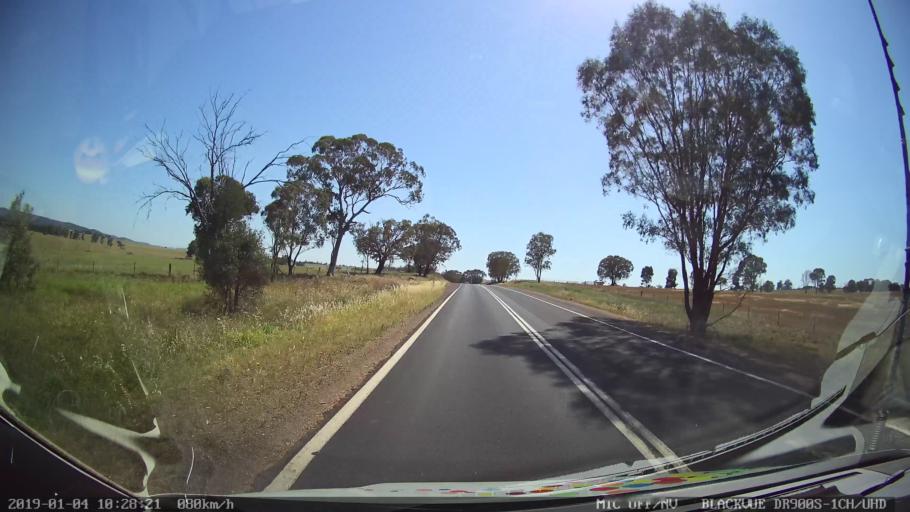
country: AU
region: New South Wales
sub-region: Cabonne
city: Canowindra
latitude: -33.3639
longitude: 148.6087
